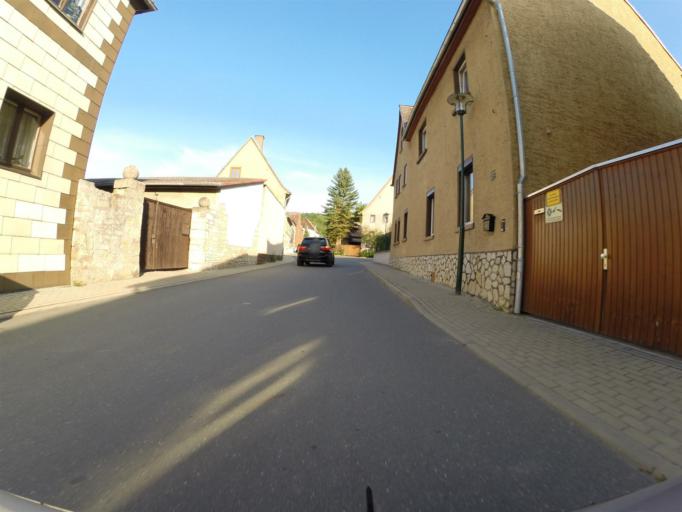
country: DE
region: Thuringia
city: Wichmar
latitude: 51.0045
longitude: 11.6736
